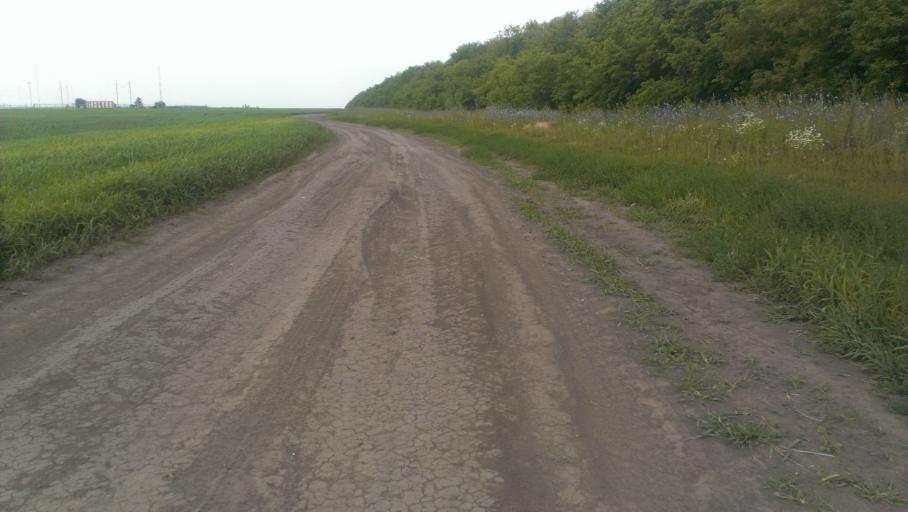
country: RU
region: Altai Krai
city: Gon'ba
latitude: 53.3830
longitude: 83.6200
